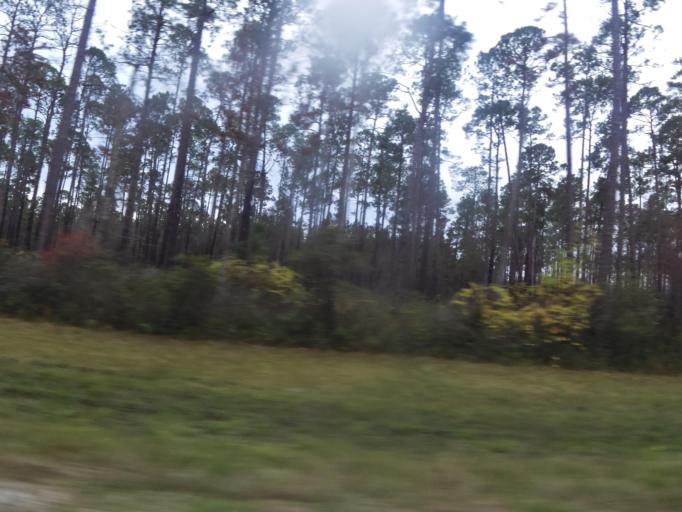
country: US
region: Georgia
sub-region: Charlton County
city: Folkston
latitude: 30.7399
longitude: -82.0928
